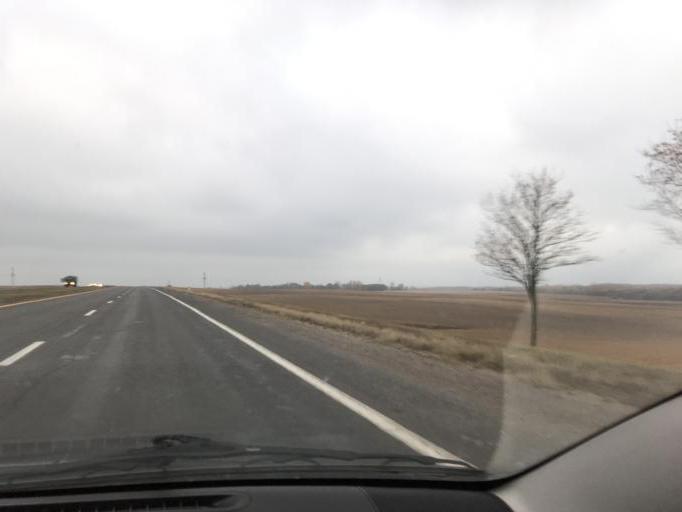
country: BY
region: Vitebsk
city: Vitebsk
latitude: 55.1542
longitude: 30.0982
